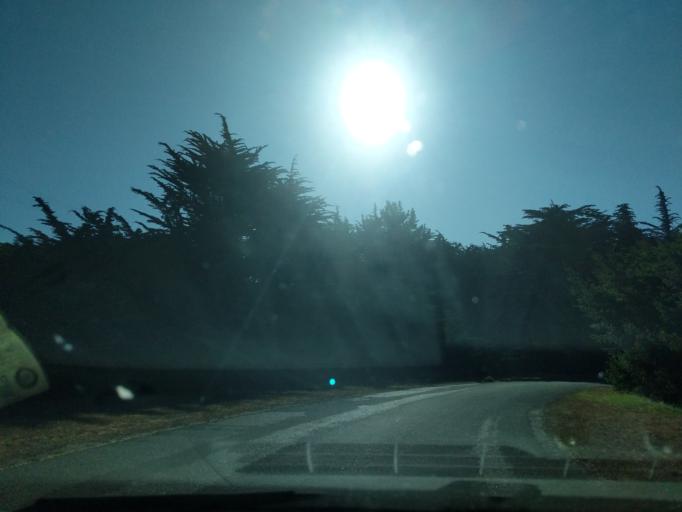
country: US
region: California
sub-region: Sonoma County
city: Monte Rio
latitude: 38.5168
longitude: -123.2469
